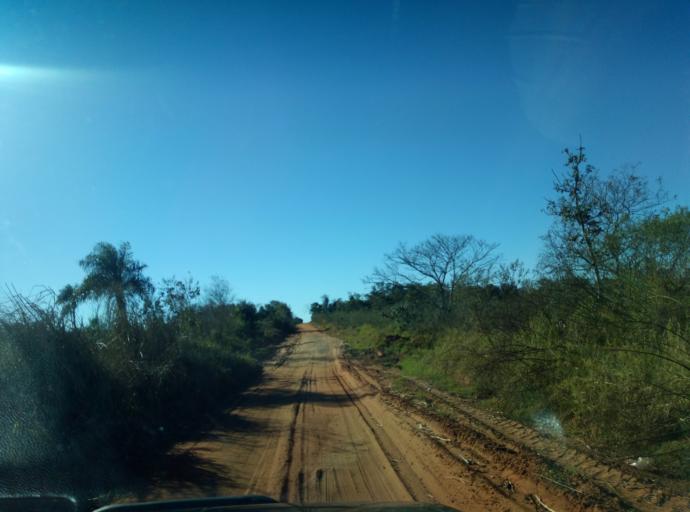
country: PY
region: Caaguazu
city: Doctor Cecilio Baez
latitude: -25.1597
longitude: -56.2849
